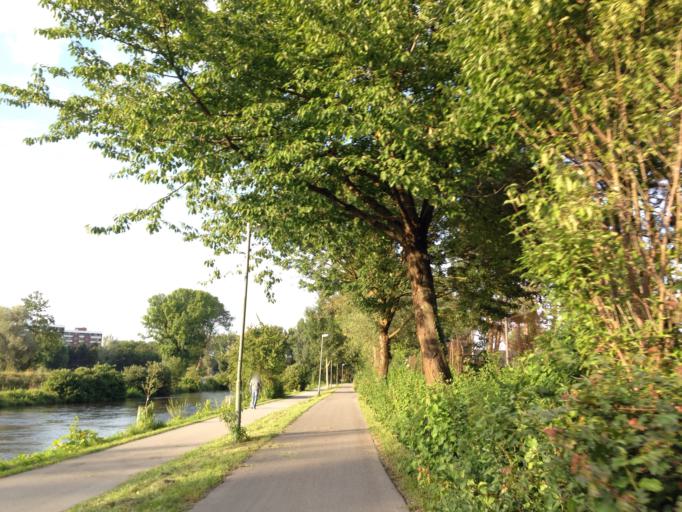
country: DE
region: Bavaria
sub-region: Swabia
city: Stadtbergen
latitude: 48.3517
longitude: 10.8694
